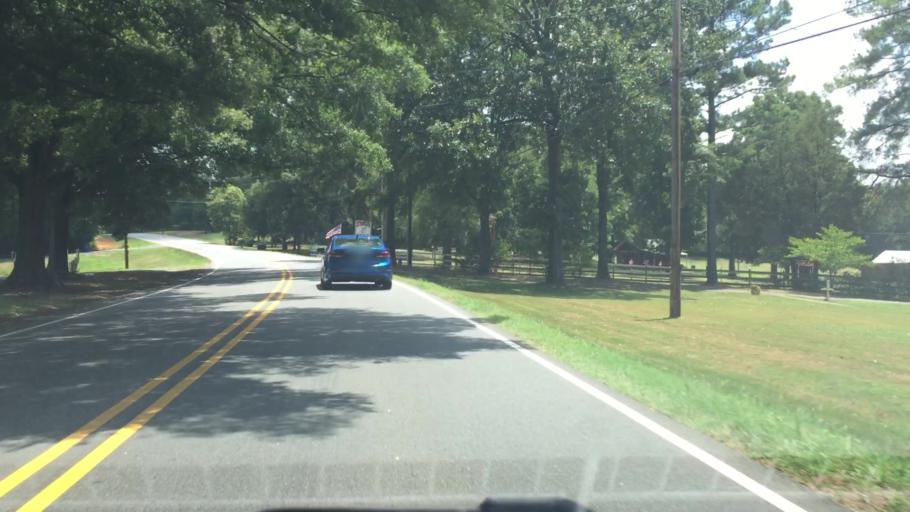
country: US
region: North Carolina
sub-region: Rowan County
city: Enochville
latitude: 35.4636
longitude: -80.7391
